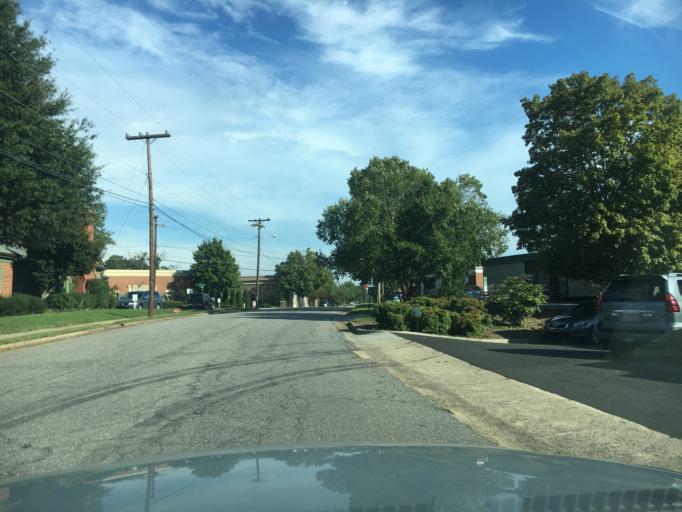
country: US
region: North Carolina
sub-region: Catawba County
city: Hickory
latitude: 35.7482
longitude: -81.3382
